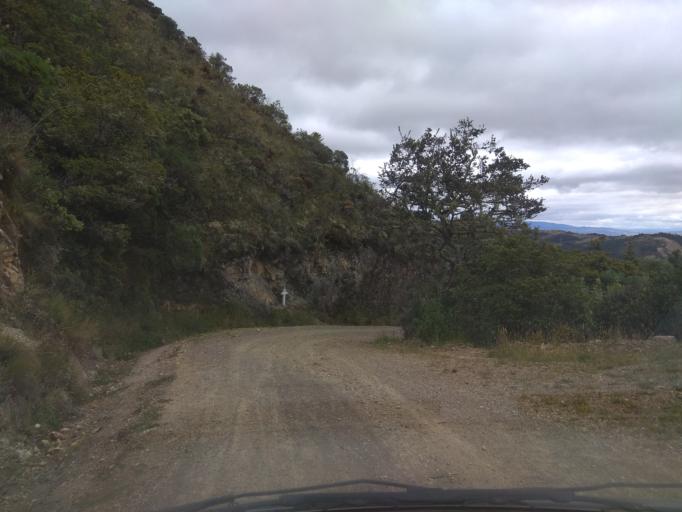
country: CO
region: Boyaca
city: Mongui
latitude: 5.7346
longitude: -72.8315
